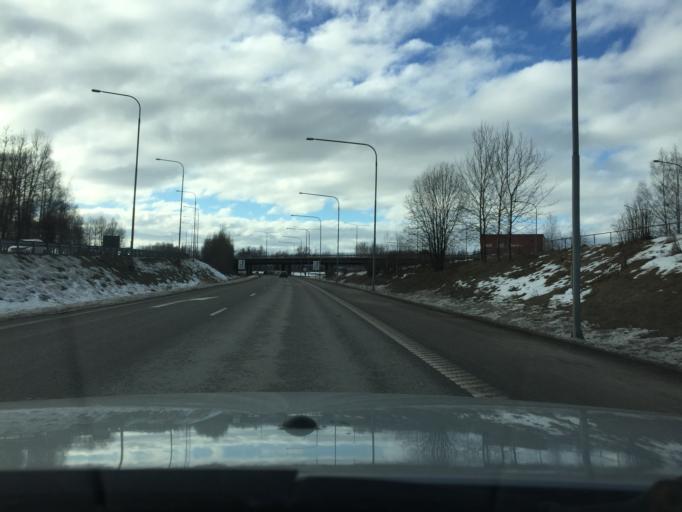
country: SE
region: OErebro
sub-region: Orebro Kommun
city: Orebro
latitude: 59.2621
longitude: 15.1730
